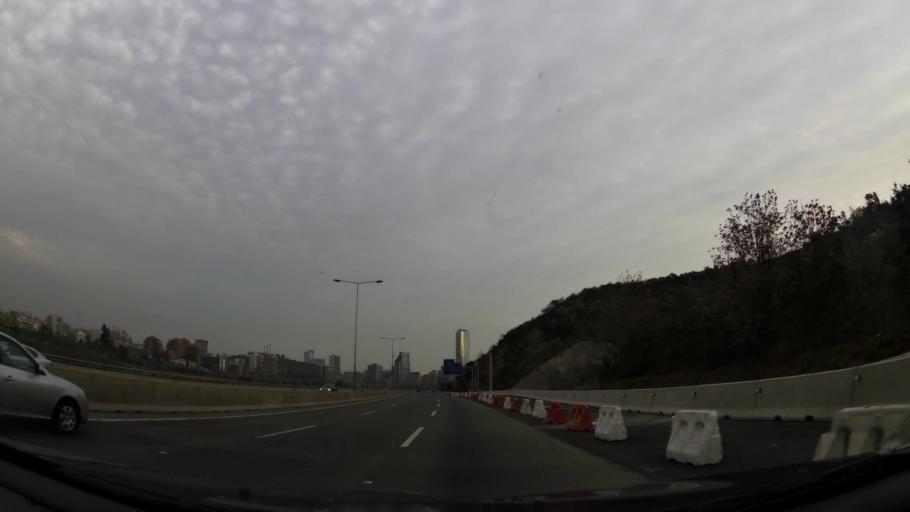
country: CL
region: Santiago Metropolitan
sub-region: Provincia de Santiago
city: Villa Presidente Frei, Nunoa, Santiago, Chile
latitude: -33.4008
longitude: -70.6045
